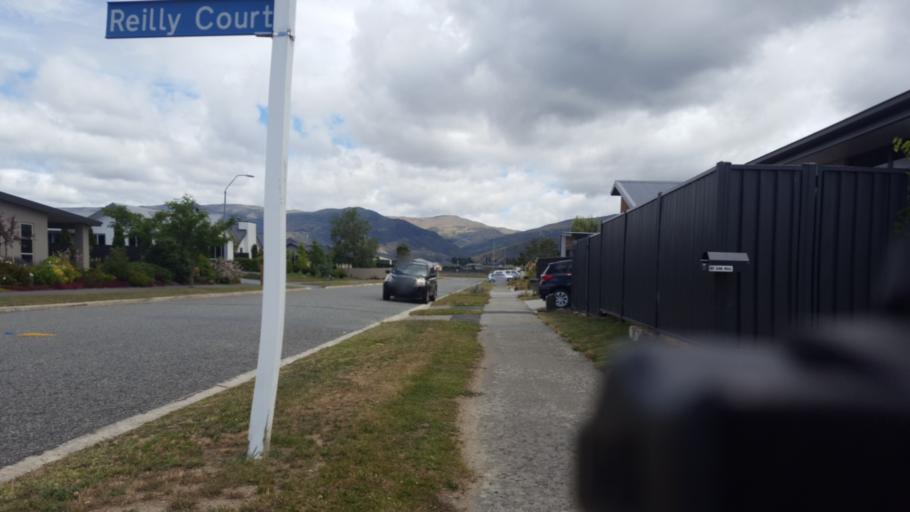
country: NZ
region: Otago
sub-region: Queenstown-Lakes District
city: Wanaka
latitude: -45.0437
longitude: 169.1821
